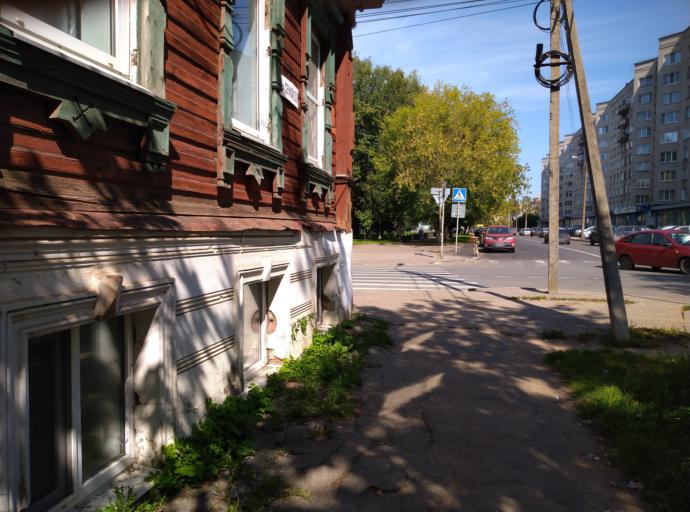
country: RU
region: Kostroma
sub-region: Kostromskoy Rayon
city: Kostroma
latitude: 57.7712
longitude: 40.9382
